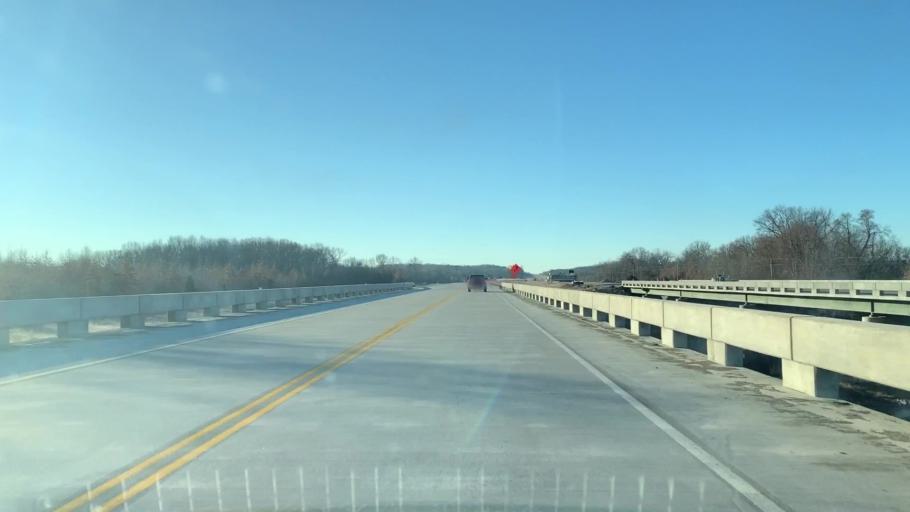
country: US
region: Kansas
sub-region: Crawford County
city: Arma
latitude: 37.6814
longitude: -94.7033
